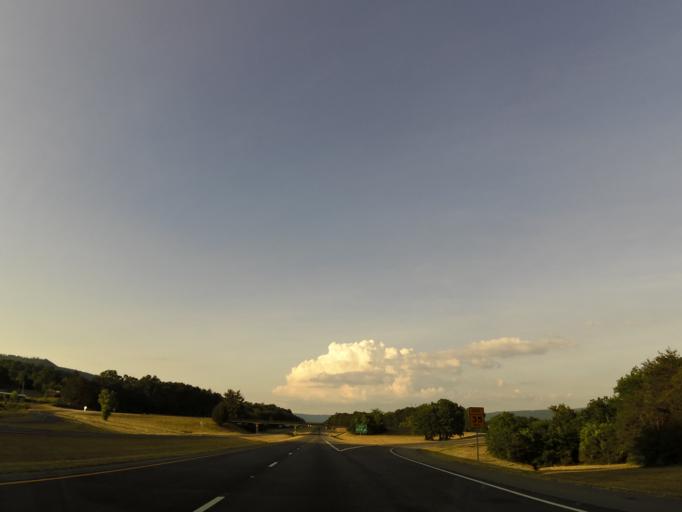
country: US
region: Georgia
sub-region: Dade County
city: Trenton
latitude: 34.6943
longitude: -85.5711
